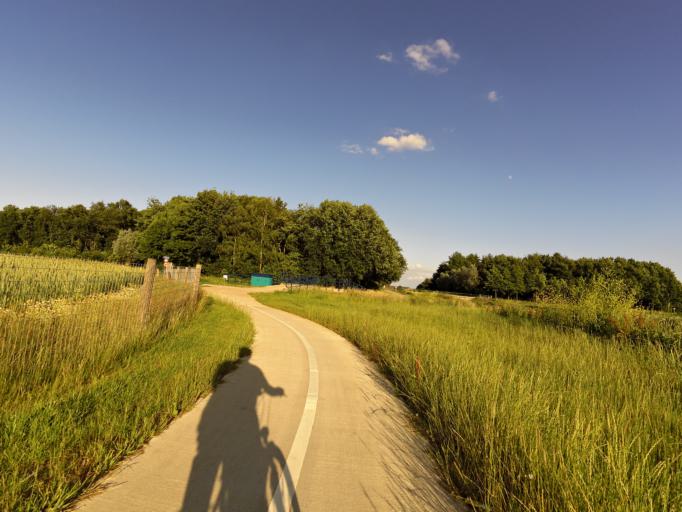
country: NL
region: Gelderland
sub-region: Oude IJsselstreek
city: Gendringen
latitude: 51.8801
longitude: 6.4111
